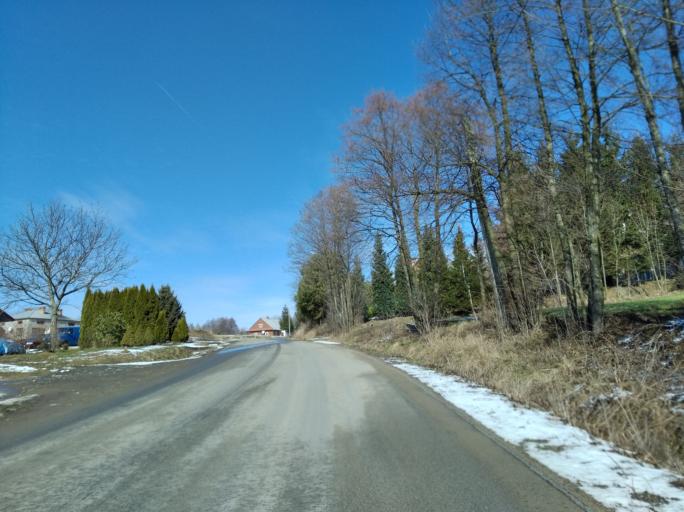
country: PL
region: Subcarpathian Voivodeship
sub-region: Powiat brzozowski
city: Jablonica Polska
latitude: 49.7204
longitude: 21.8801
